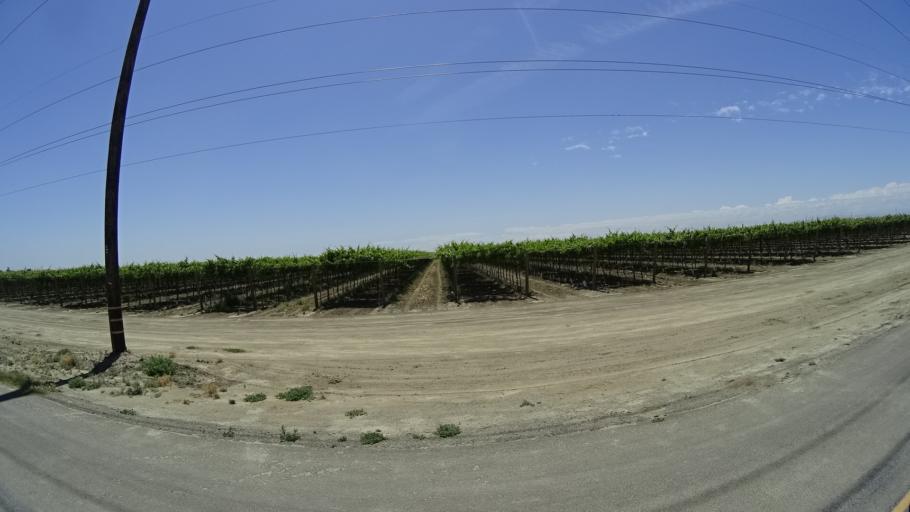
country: US
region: California
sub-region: Kings County
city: Stratford
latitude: 36.2406
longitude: -119.8273
